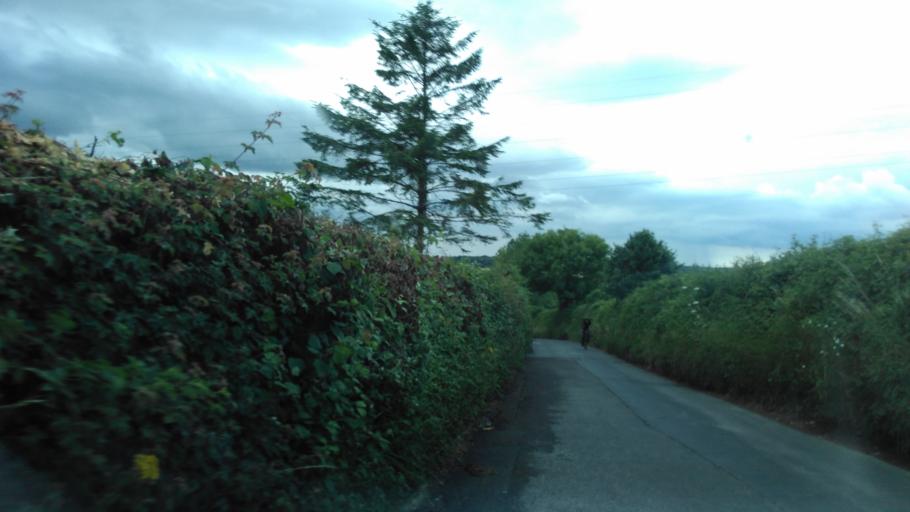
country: GB
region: England
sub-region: Kent
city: Chartham
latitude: 51.2504
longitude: 1.0238
